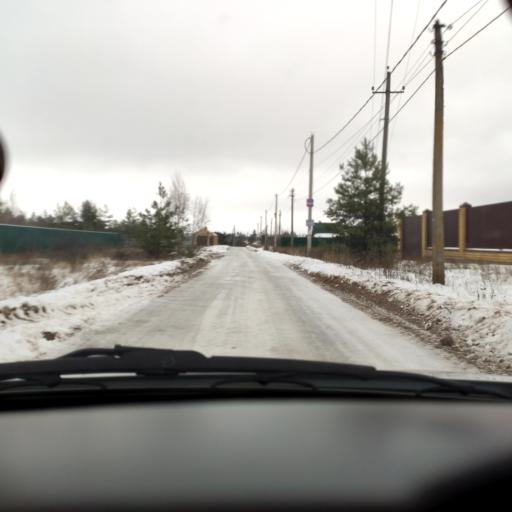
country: RU
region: Voronezj
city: Ramon'
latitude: 51.8842
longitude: 39.2612
